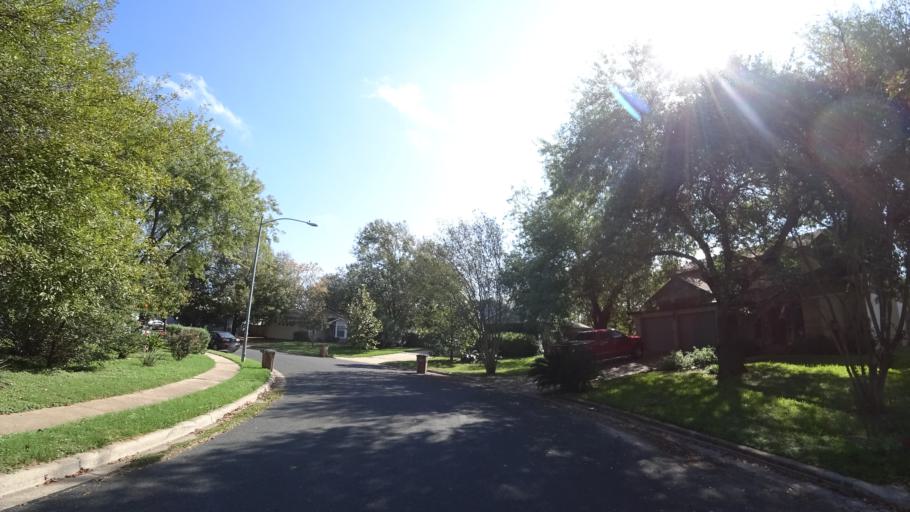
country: US
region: Texas
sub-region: Travis County
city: Shady Hollow
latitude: 30.1962
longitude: -97.8225
